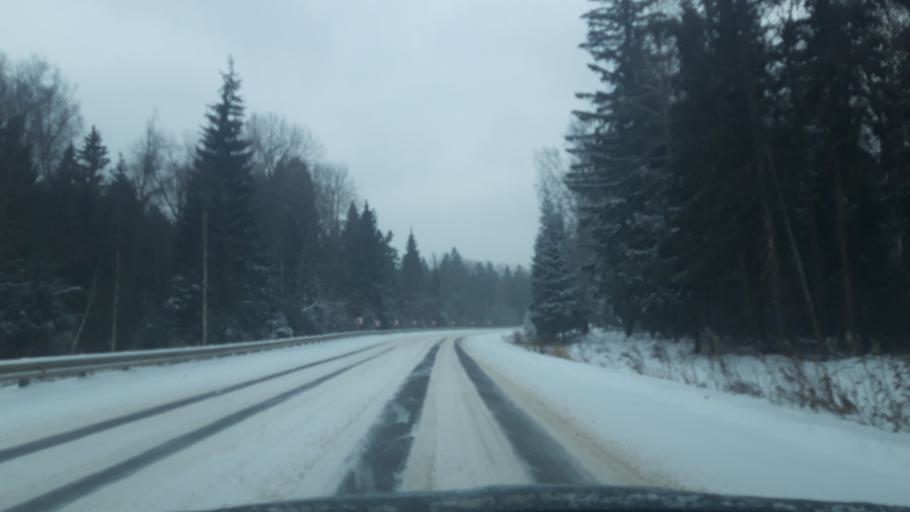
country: RU
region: Moskovskaya
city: Avtopoligon
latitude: 56.2818
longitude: 37.3758
